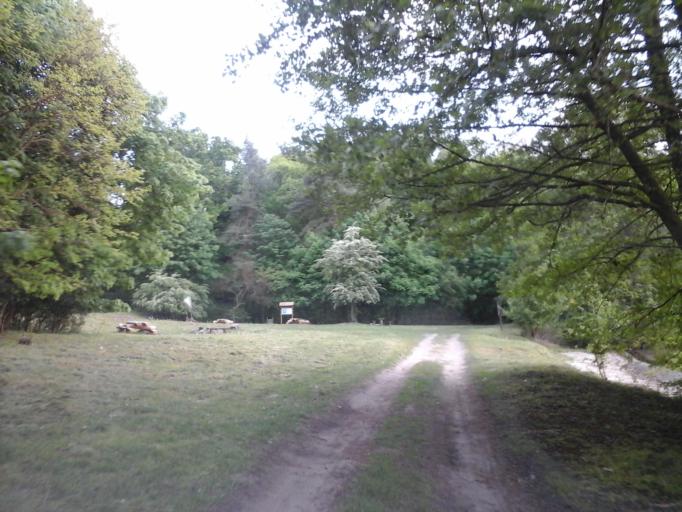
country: PL
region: West Pomeranian Voivodeship
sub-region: Powiat choszczenski
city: Pelczyce
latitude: 52.9839
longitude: 15.3725
